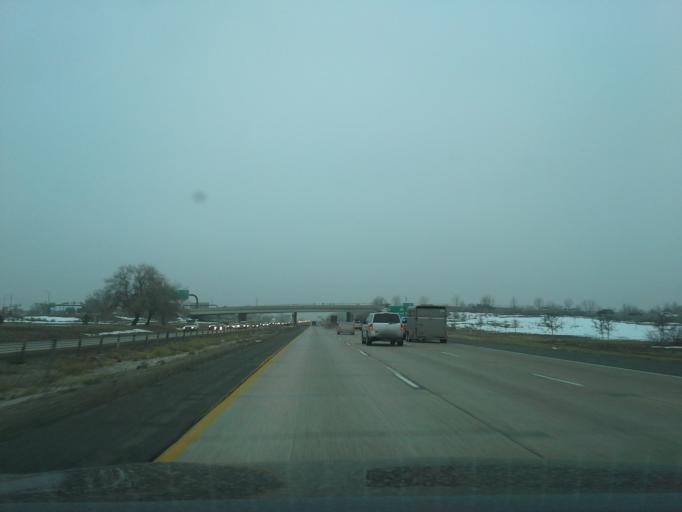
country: US
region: Utah
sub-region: Davis County
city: Hill Air Force Bace
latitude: 41.0912
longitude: -111.9928
